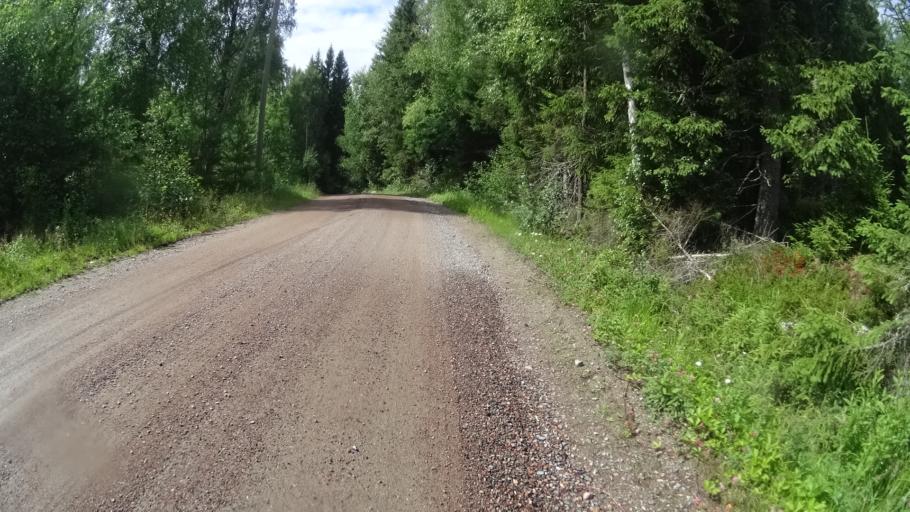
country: FI
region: Uusimaa
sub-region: Helsinki
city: Karkkila
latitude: 60.5865
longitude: 24.3164
